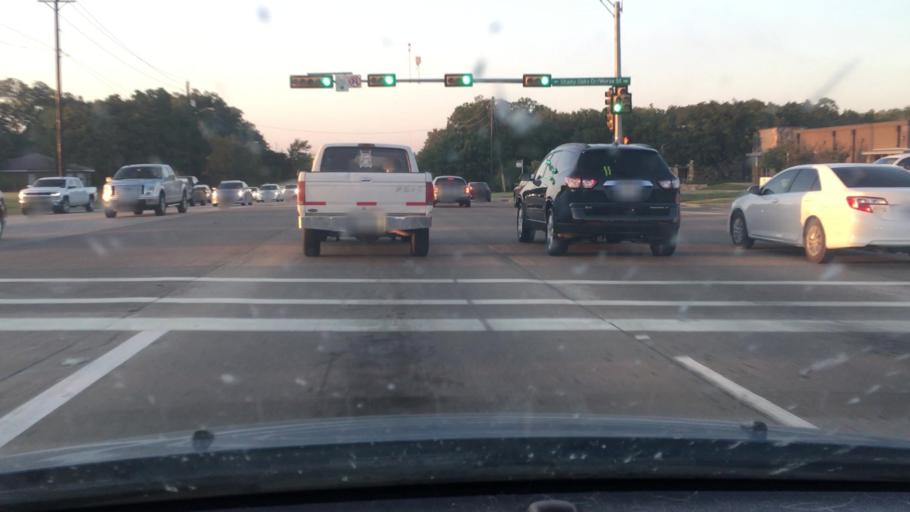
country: US
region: Texas
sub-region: Denton County
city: Denton
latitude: 33.2046
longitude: -97.0909
